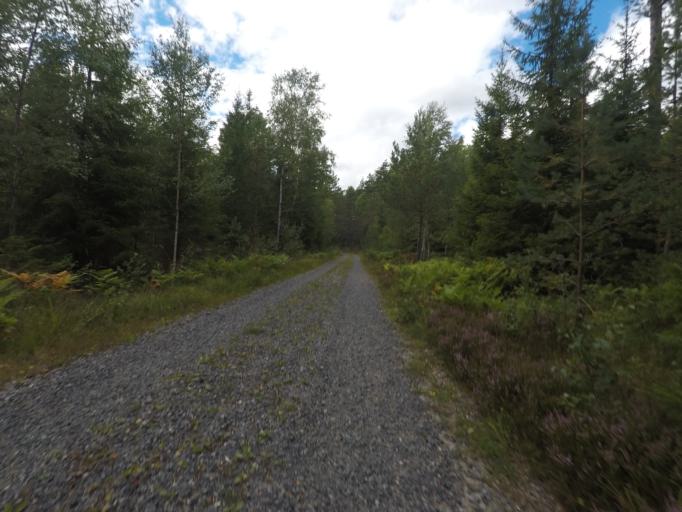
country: SE
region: Soedermanland
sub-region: Eskilstuna Kommun
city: Kvicksund
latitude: 59.4012
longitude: 16.2809
